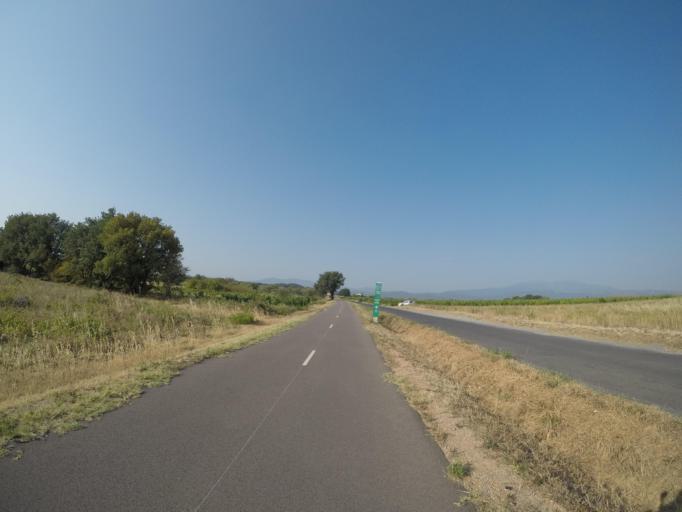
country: FR
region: Languedoc-Roussillon
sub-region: Departement des Pyrenees-Orientales
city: Ponteilla
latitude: 42.6331
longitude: 2.8072
